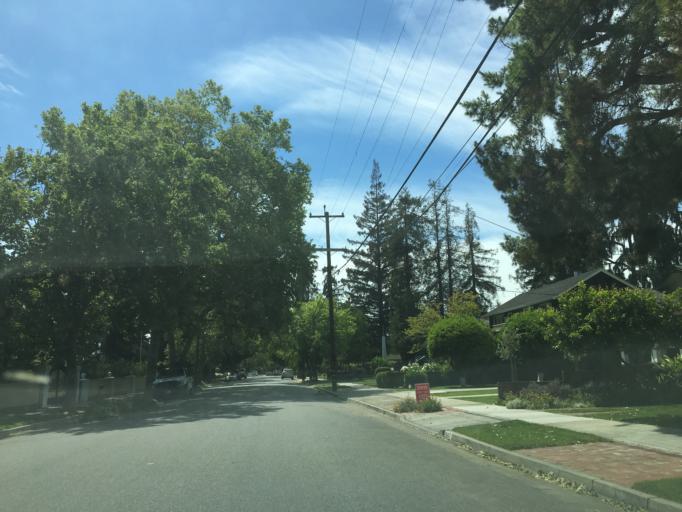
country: US
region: California
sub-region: Santa Clara County
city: Buena Vista
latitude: 37.3004
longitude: -121.9001
